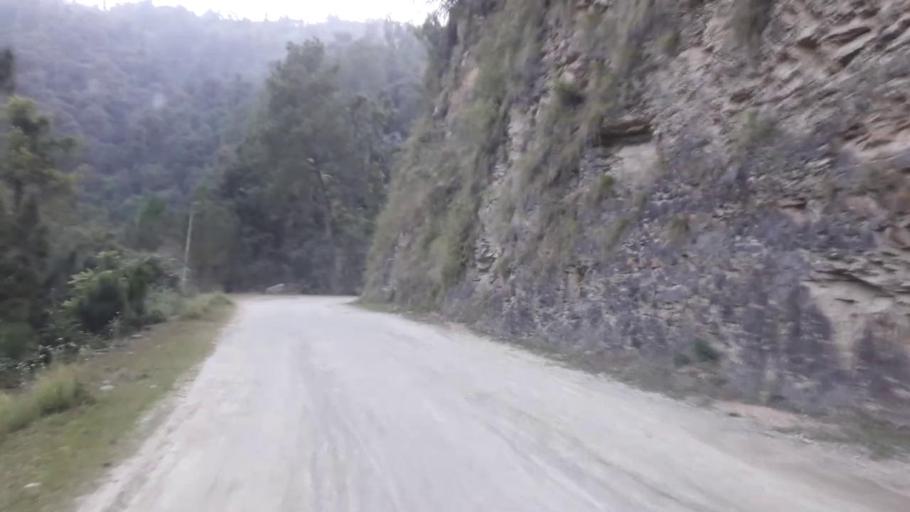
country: IN
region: Himachal Pradesh
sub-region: Shimla
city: Shimla
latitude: 31.0581
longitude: 77.1504
